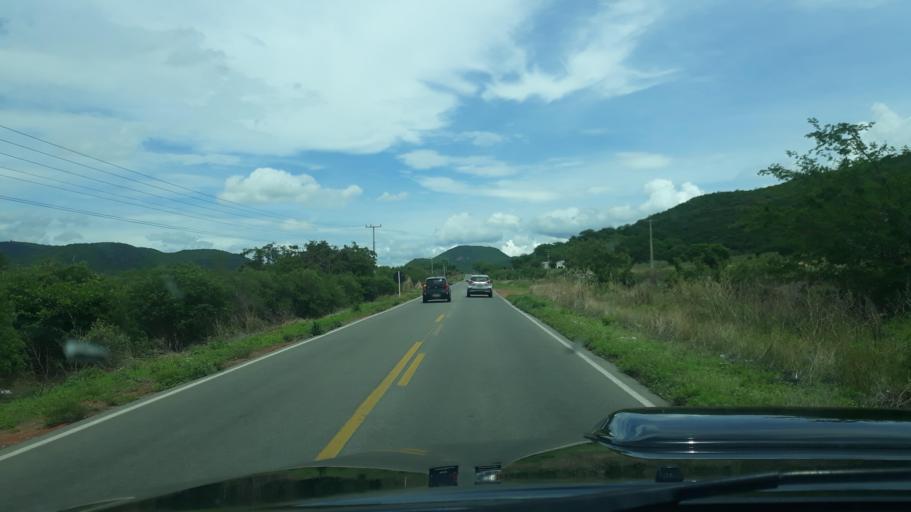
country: BR
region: Bahia
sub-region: Guanambi
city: Guanambi
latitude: -14.2558
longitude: -42.7344
